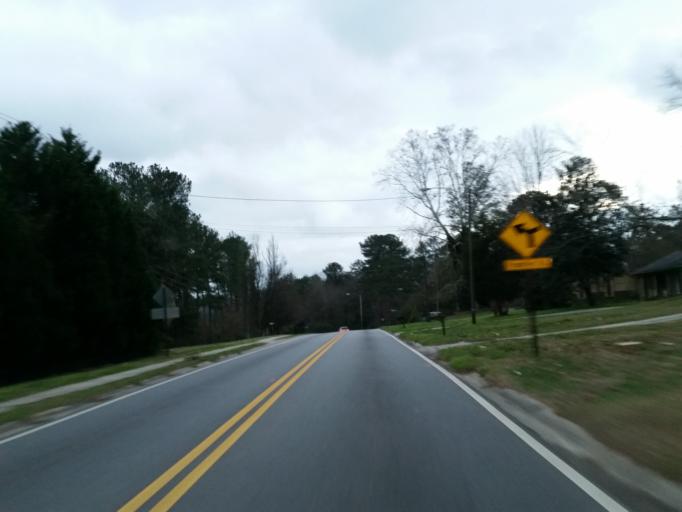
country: US
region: Georgia
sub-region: Cobb County
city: Fair Oaks
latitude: 33.8757
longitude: -84.5798
